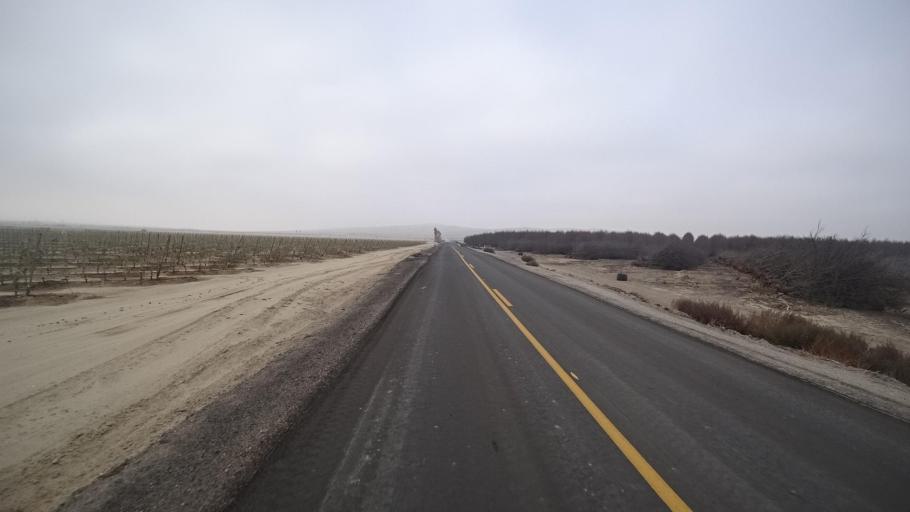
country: US
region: California
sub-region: Kern County
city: Maricopa
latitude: 35.1180
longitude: -119.3565
